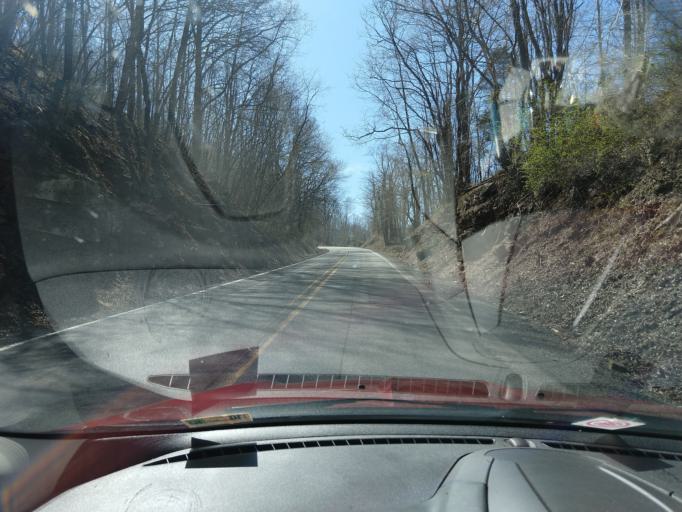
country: US
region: West Virginia
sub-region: Summers County
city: Hinton
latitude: 37.7603
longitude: -80.8916
